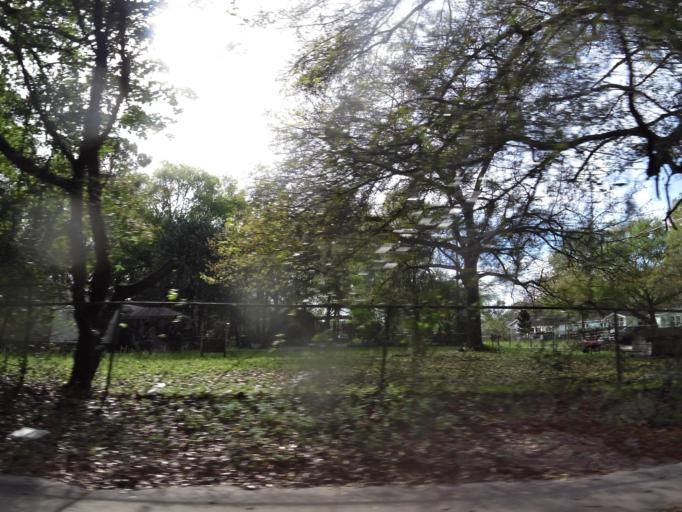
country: US
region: Florida
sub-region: Clay County
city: Bellair-Meadowbrook Terrace
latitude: 30.2540
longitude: -81.7859
